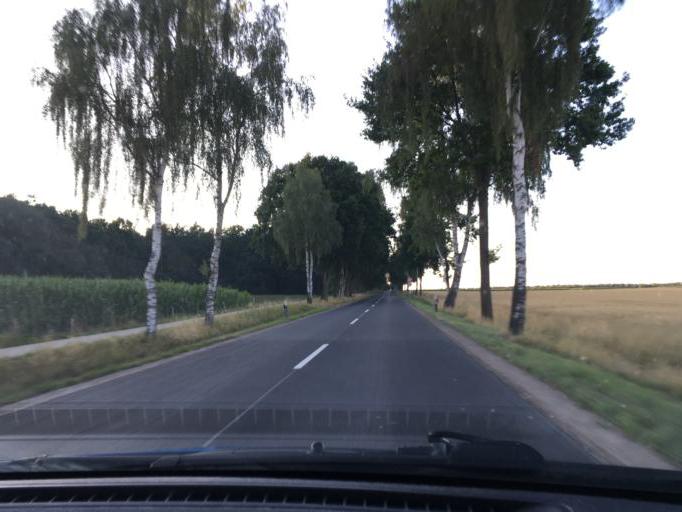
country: DE
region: Lower Saxony
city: Eimke
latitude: 52.9794
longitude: 10.3089
